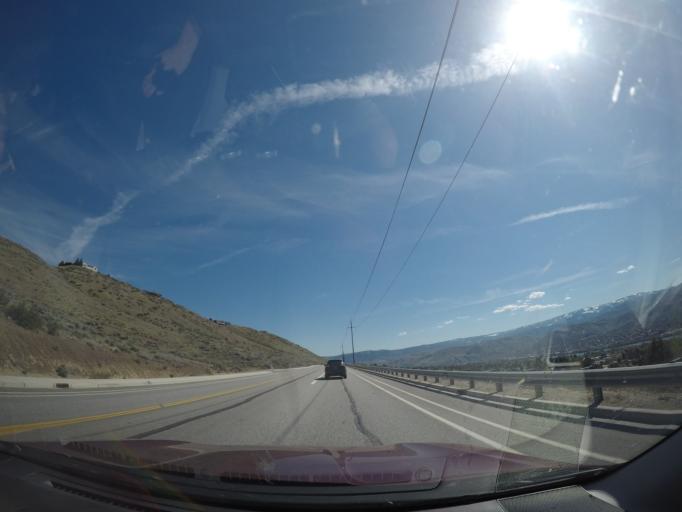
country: US
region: Washington
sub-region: Douglas County
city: East Wenatchee Bench
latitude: 47.4517
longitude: -120.2892
